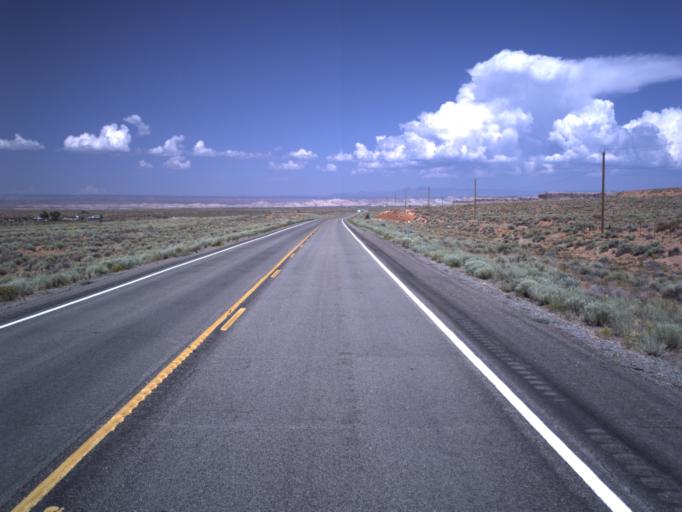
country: US
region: Utah
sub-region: San Juan County
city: Blanding
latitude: 37.1477
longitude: -109.5639
